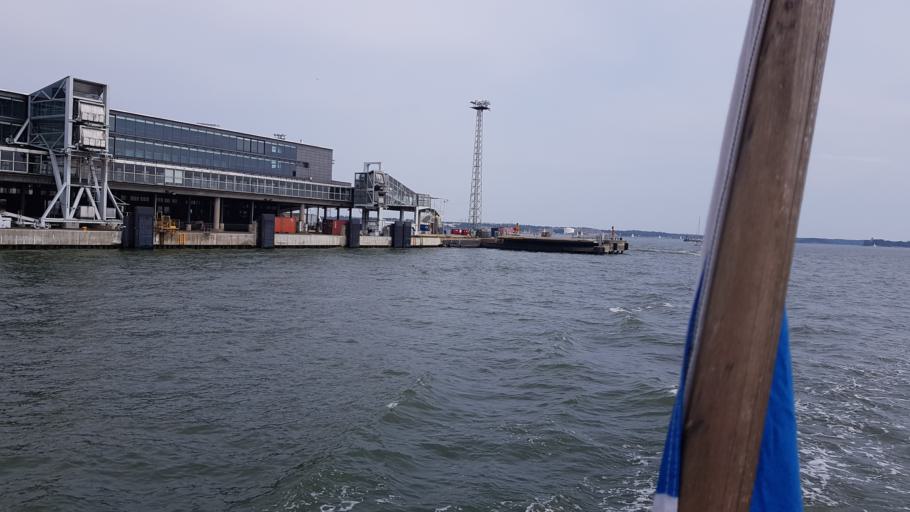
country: FI
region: Uusimaa
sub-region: Helsinki
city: Helsinki
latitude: 60.1630
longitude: 24.9671
